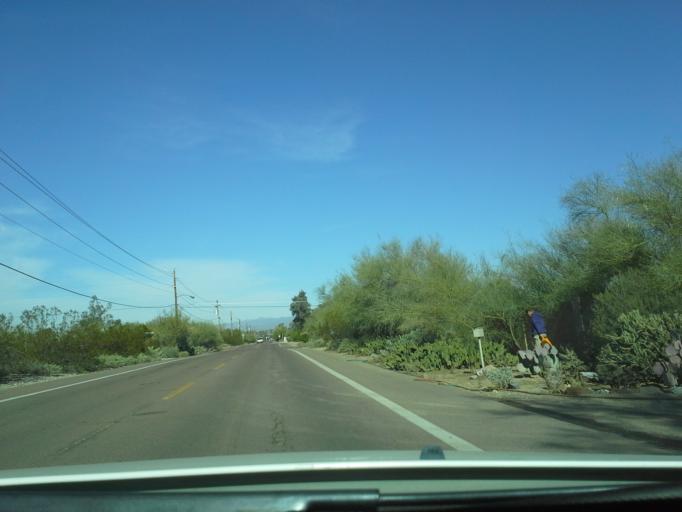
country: US
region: Arizona
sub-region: Maricopa County
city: Paradise Valley
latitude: 33.5764
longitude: -111.9957
